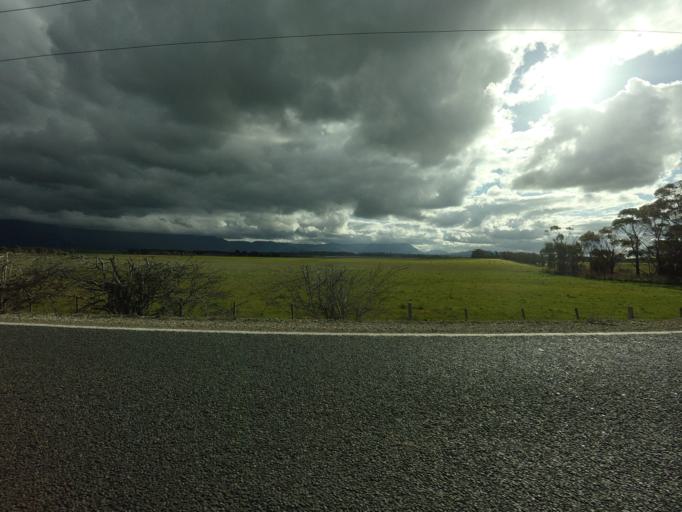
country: AU
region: Tasmania
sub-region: Northern Midlands
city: Longford
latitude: -41.7421
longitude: 147.0822
